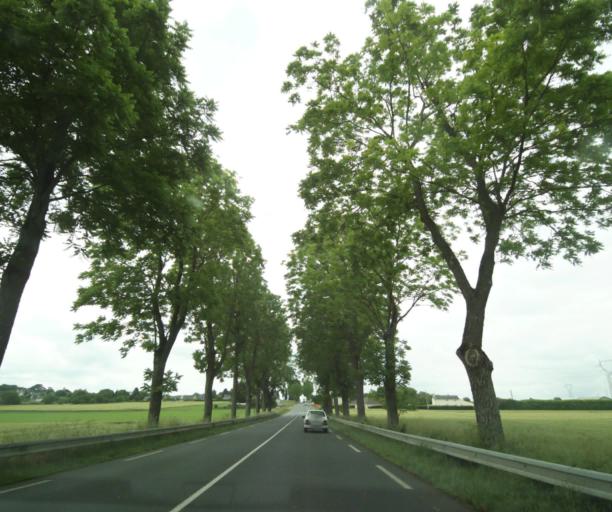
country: FR
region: Pays de la Loire
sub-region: Departement de Maine-et-Loire
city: Distre
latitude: 47.2023
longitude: -0.1220
